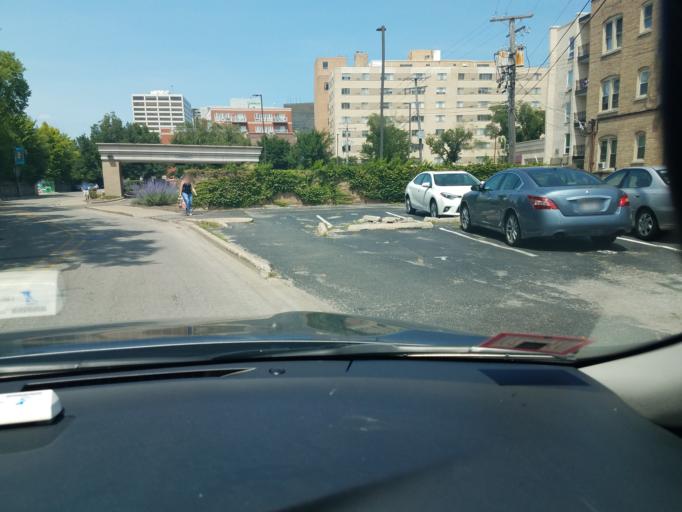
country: US
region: Illinois
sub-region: Cook County
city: Evanston
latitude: 42.0418
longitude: -87.6815
